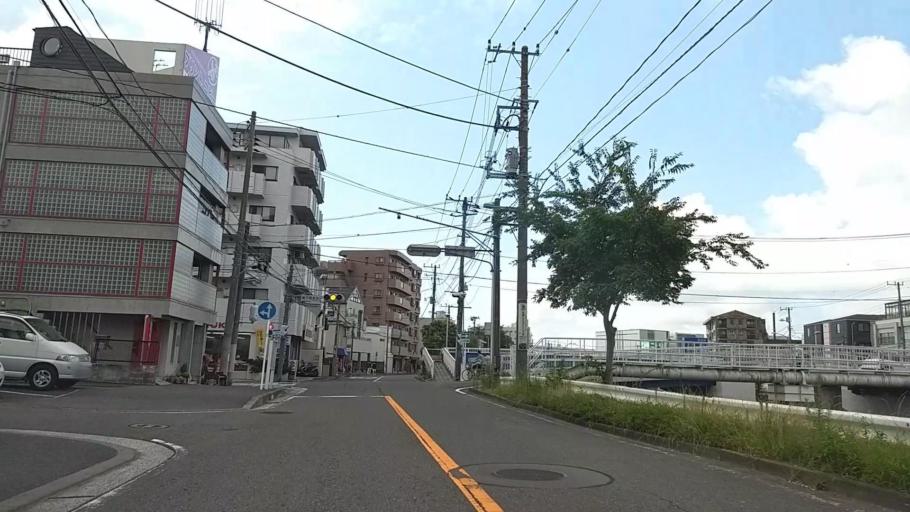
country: JP
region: Kanagawa
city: Yokohama
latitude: 35.4176
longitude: 139.6269
